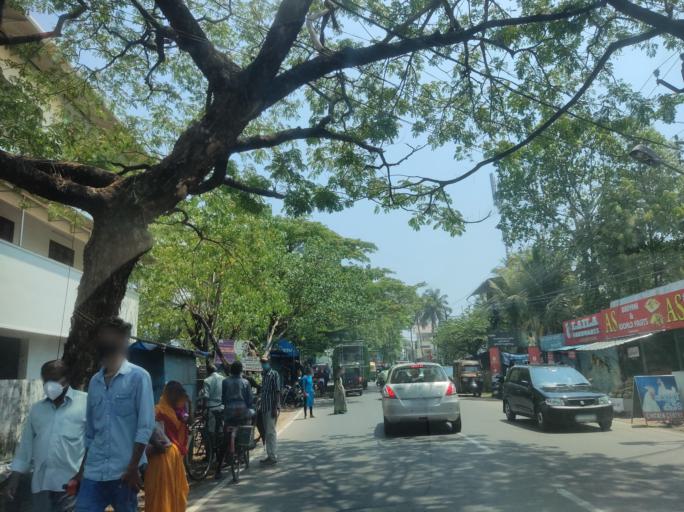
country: IN
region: Kerala
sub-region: Ernakulam
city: Cochin
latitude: 9.9037
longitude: 76.2817
